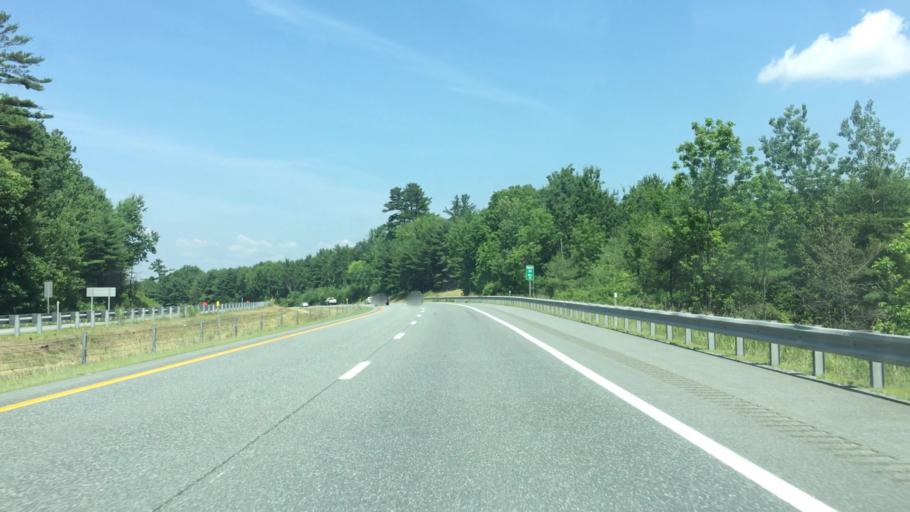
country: US
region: New Hampshire
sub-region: Grafton County
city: Lebanon
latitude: 43.6223
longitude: -72.1988
